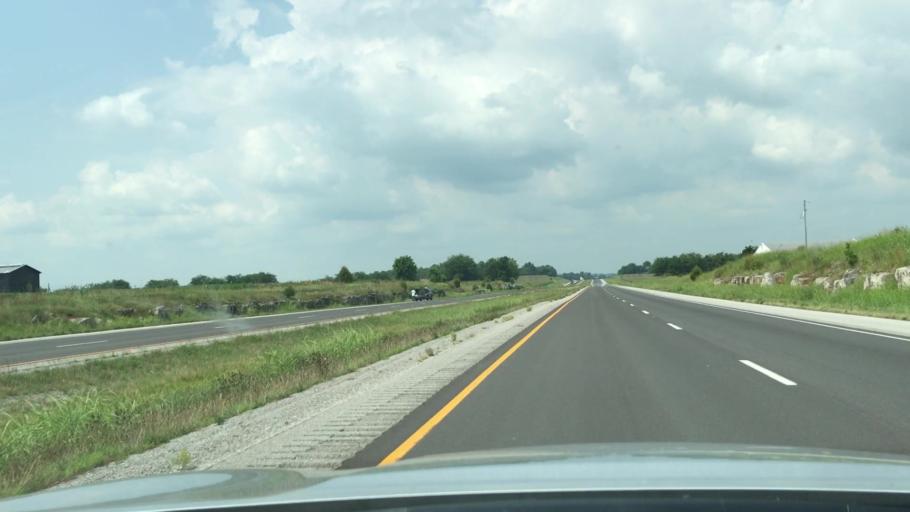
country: US
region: Kentucky
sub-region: Logan County
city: Russellville
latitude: 36.8245
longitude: -86.9875
